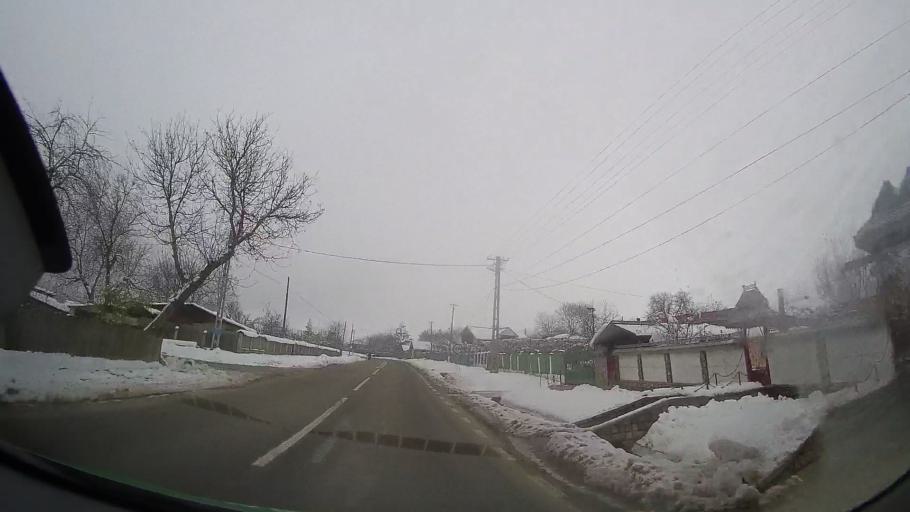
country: RO
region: Vaslui
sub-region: Comuna Todiresti
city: Todiresti
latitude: 46.8414
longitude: 27.3726
